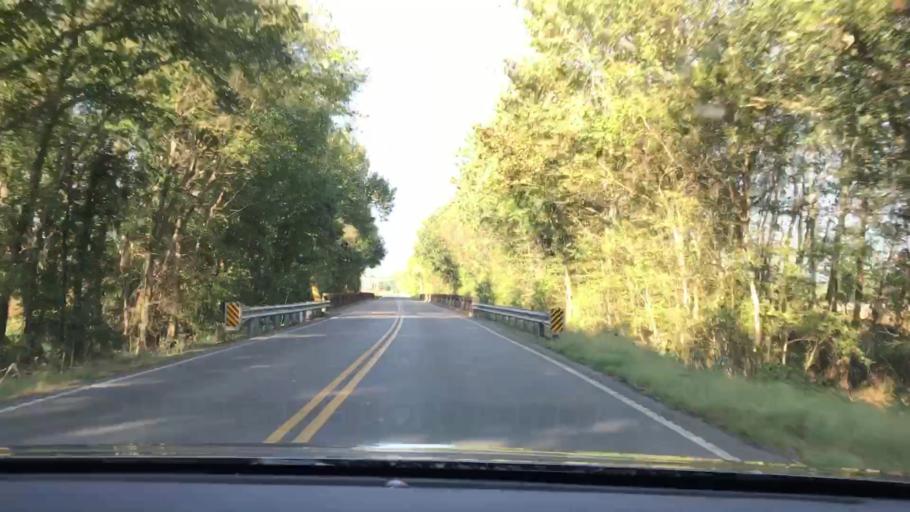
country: US
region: Kentucky
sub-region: Marshall County
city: Benton
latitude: 36.7688
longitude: -88.2811
